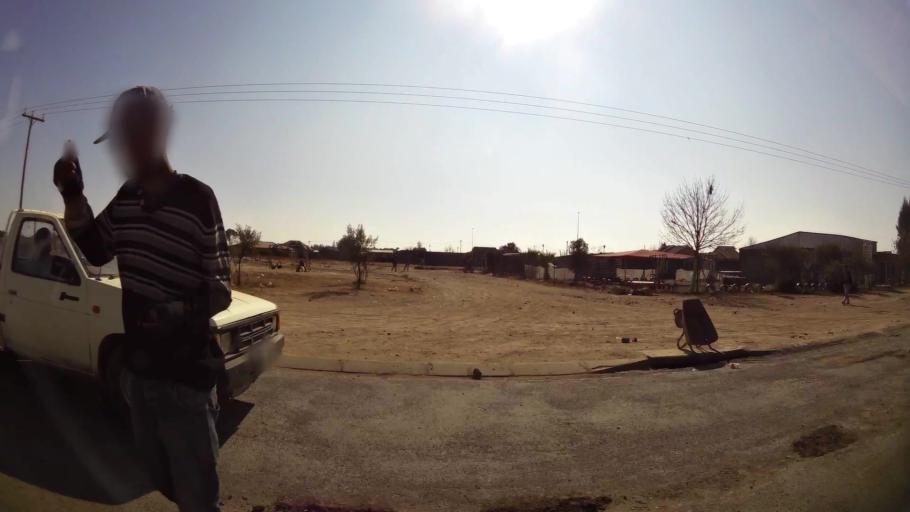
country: ZA
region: Orange Free State
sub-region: Mangaung Metropolitan Municipality
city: Bloemfontein
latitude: -29.1950
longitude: 26.2742
